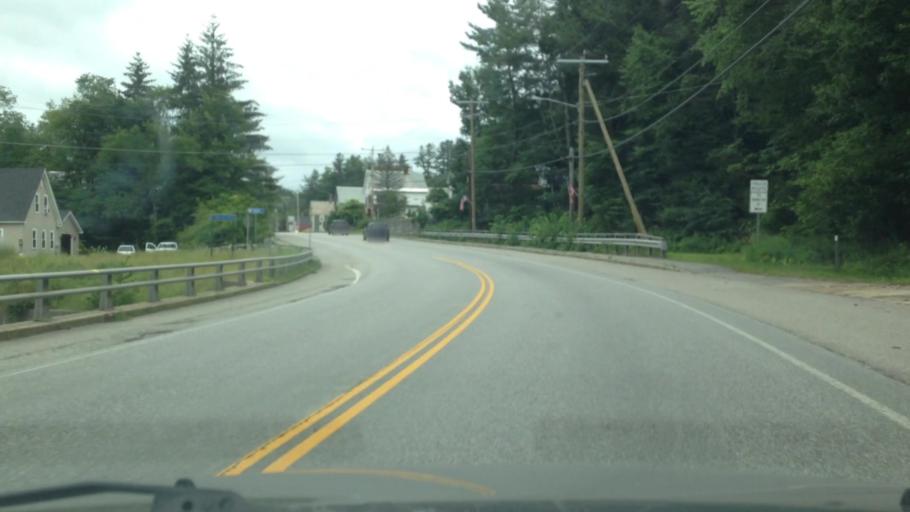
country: US
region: New Hampshire
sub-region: Cheshire County
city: Marlborough
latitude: 42.9085
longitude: -72.2170
